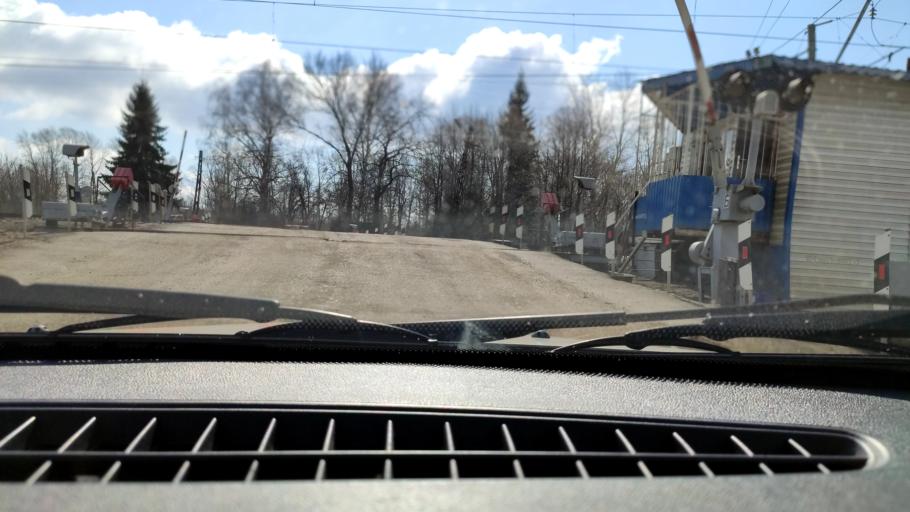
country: RU
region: Bashkortostan
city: Kudeyevskiy
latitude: 54.8664
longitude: 56.7412
